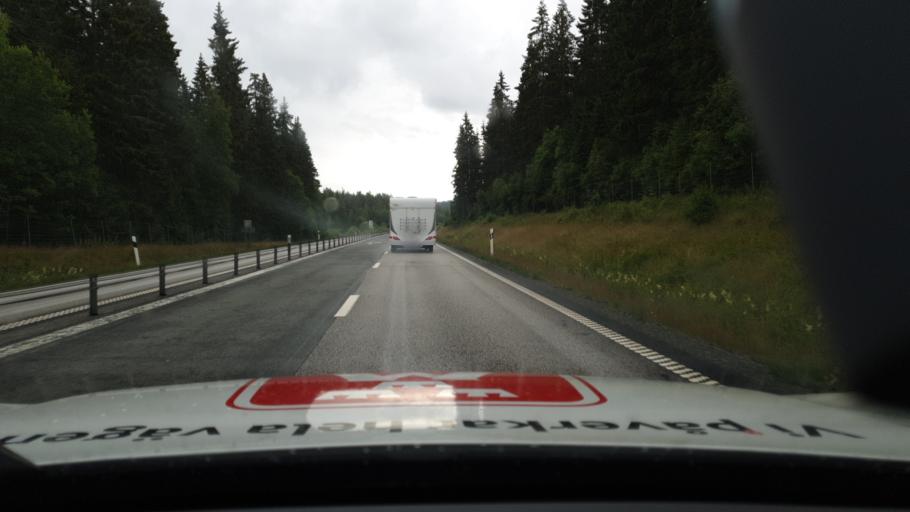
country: SE
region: Joenkoeping
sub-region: Nassjo Kommun
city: Malmback
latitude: 57.6997
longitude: 14.4384
